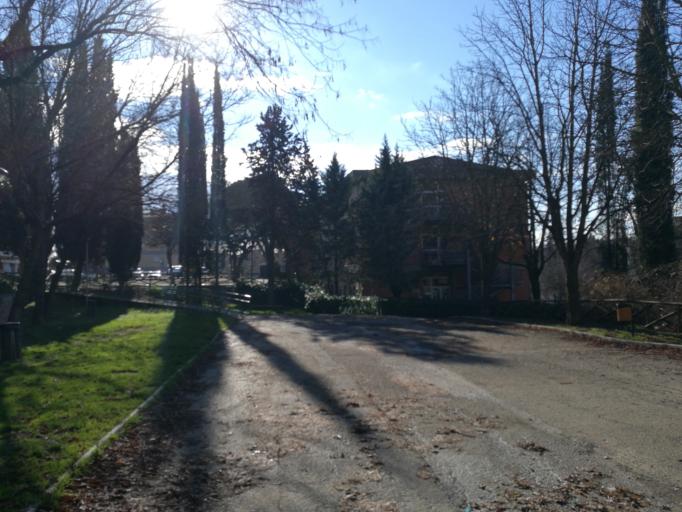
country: IT
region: Umbria
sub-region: Provincia di Perugia
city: Perugia
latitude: 43.1010
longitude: 12.3897
